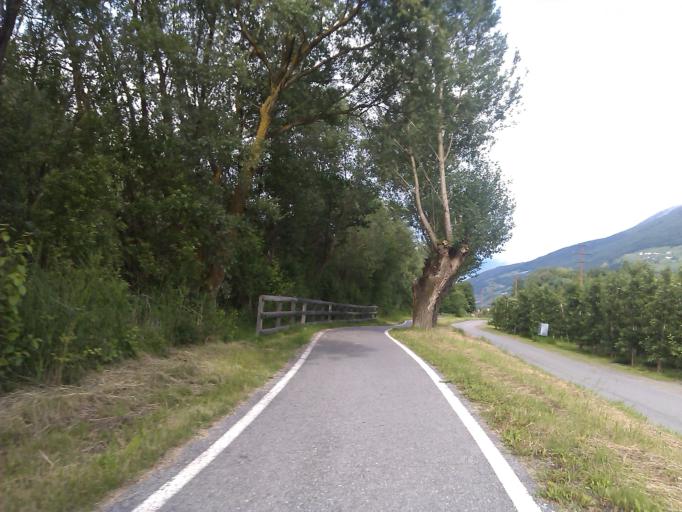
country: IT
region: Trentino-Alto Adige
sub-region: Bolzano
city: Lasa
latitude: 46.6211
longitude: 10.6569
